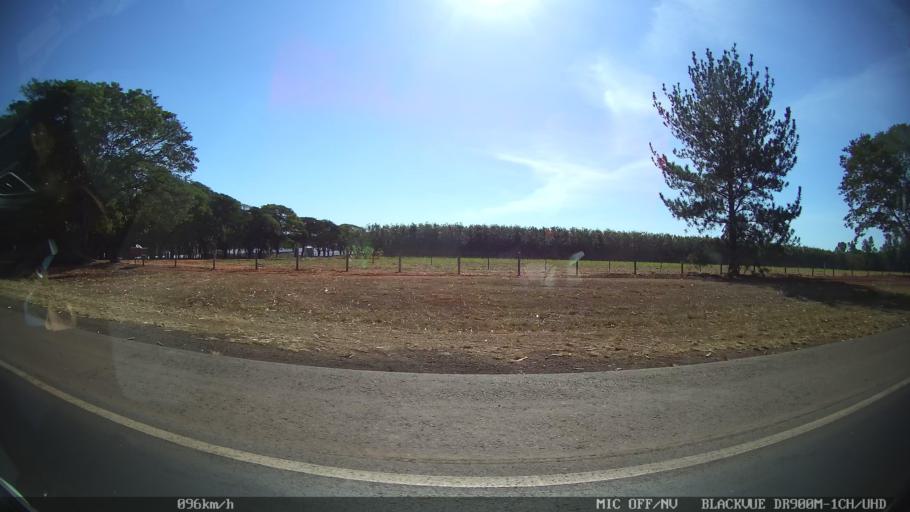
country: BR
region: Sao Paulo
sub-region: Olimpia
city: Olimpia
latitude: -20.6714
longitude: -48.8768
